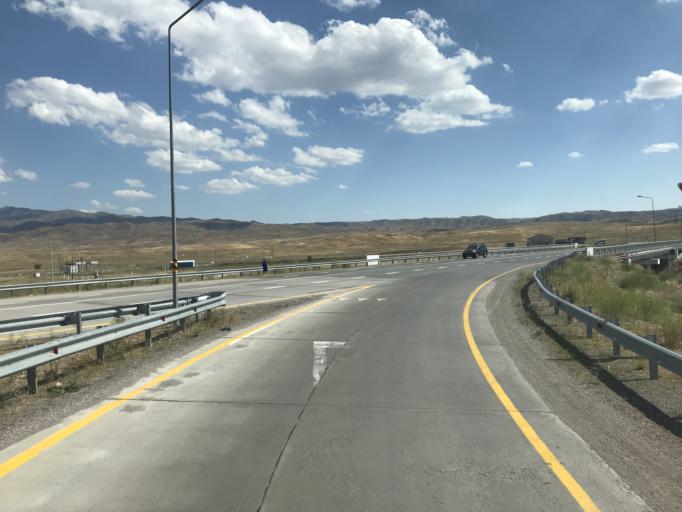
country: KG
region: Chuy
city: Ivanovka
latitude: 43.4098
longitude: 75.0882
